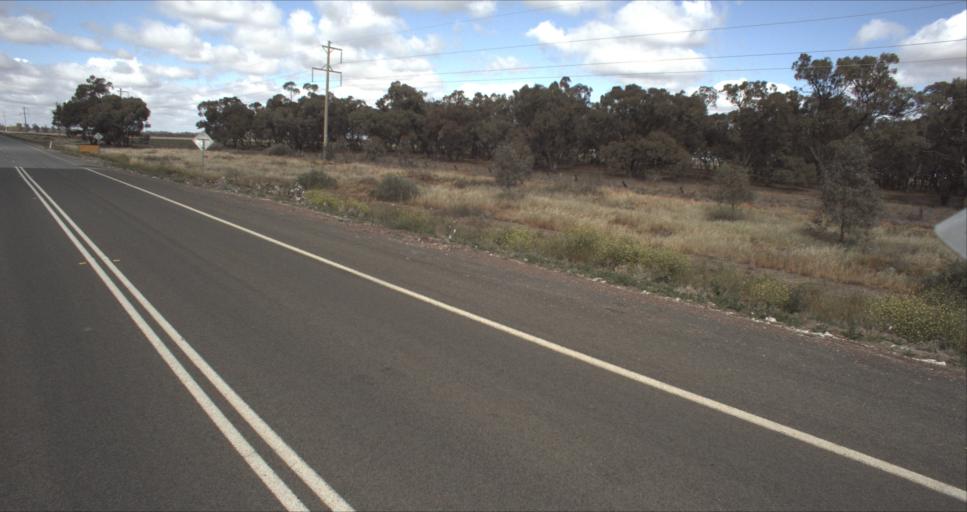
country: AU
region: New South Wales
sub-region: Murrumbidgee Shire
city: Darlington Point
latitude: -34.5752
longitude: 146.1663
